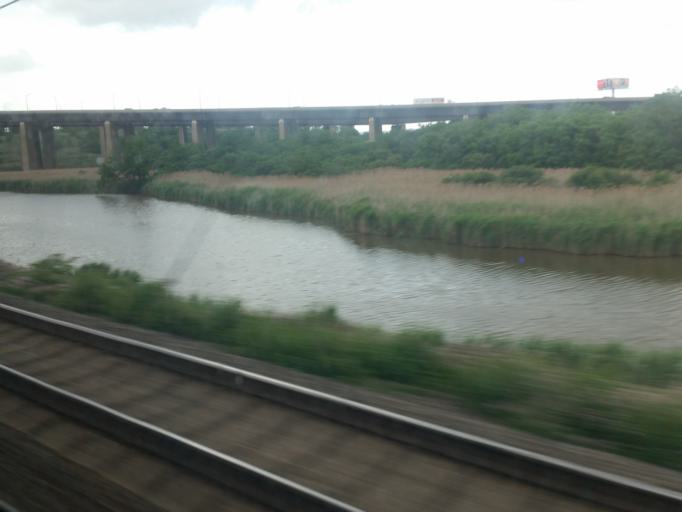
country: US
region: New Jersey
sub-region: Hudson County
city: Kearny
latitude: 40.7465
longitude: -74.1159
